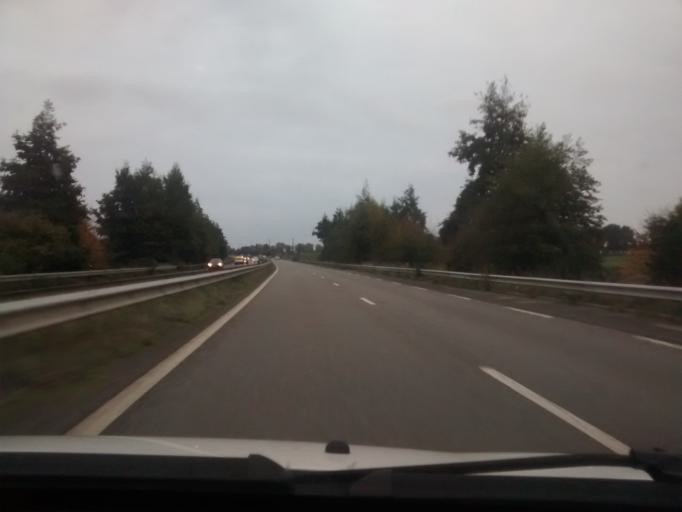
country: FR
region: Brittany
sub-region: Departement d'Ille-et-Vilaine
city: La Meziere
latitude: 48.2334
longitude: -1.7572
